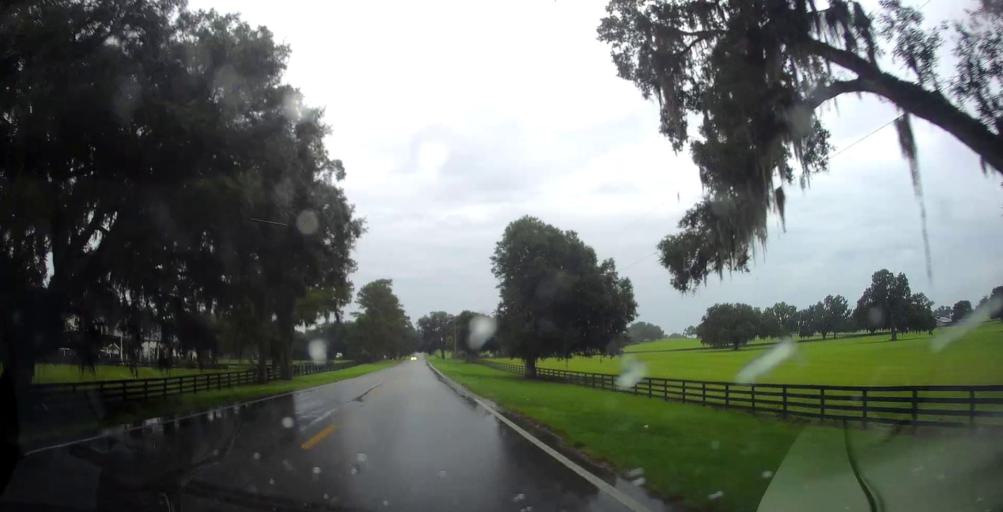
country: US
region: Florida
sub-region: Marion County
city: Citra
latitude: 29.3539
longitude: -82.2341
